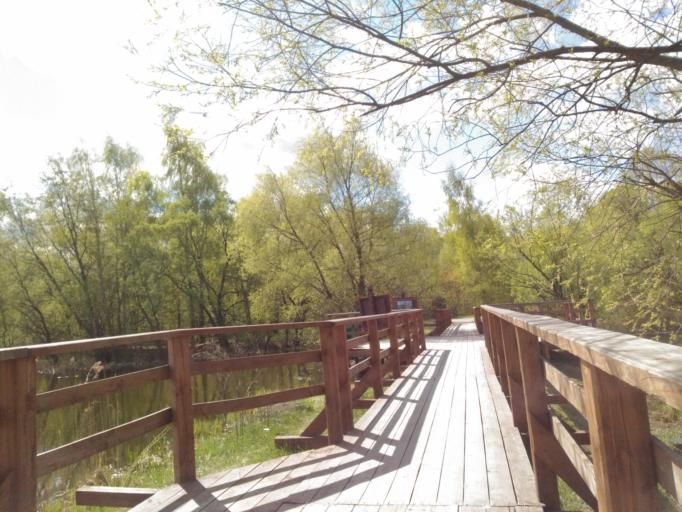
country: RU
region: Moscow
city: Shchukino
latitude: 55.7776
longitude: 37.4297
